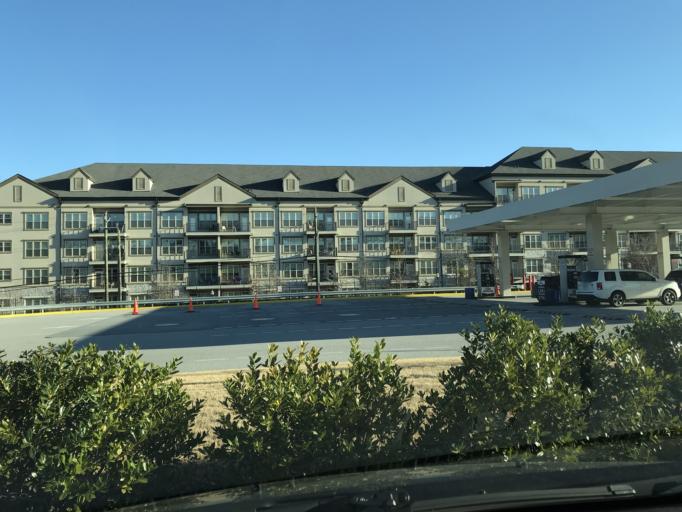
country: US
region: Georgia
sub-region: DeKalb County
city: North Atlanta
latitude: 33.8732
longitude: -84.3366
